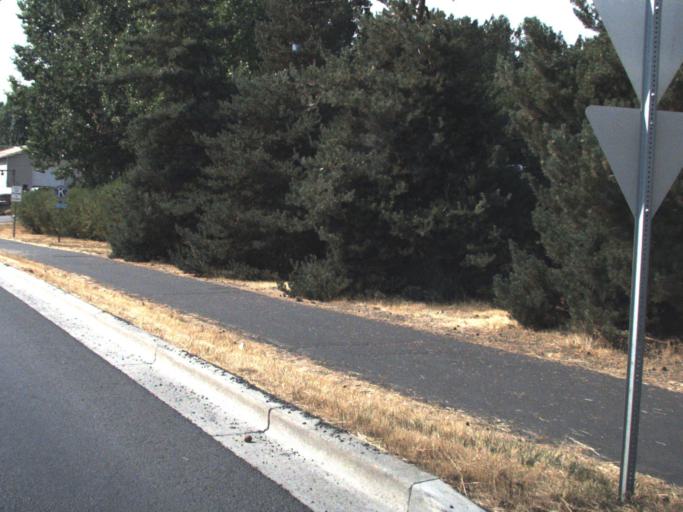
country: US
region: Washington
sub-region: Whitman County
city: Pullman
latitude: 46.7498
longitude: -117.1720
